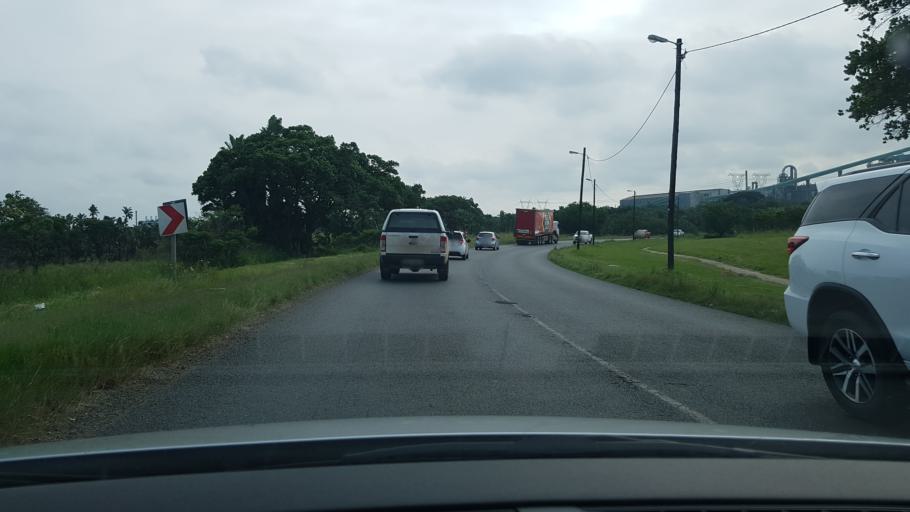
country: ZA
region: KwaZulu-Natal
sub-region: uThungulu District Municipality
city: Richards Bay
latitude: -28.7619
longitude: 32.0427
